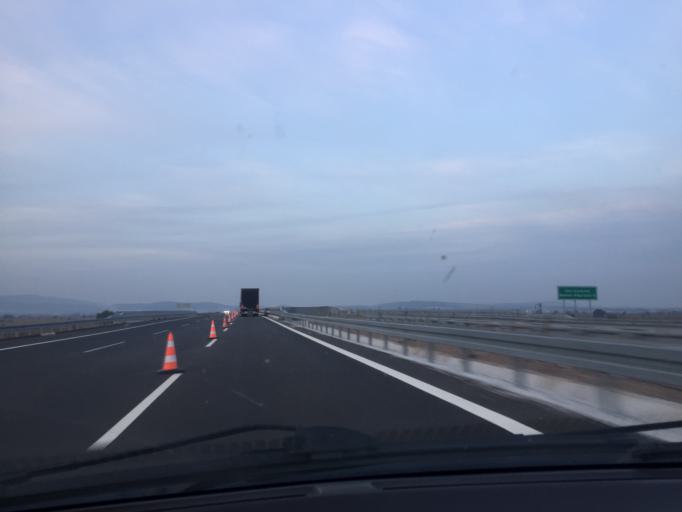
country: TR
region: Manisa
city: Halitpasa
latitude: 38.7344
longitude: 27.6566
